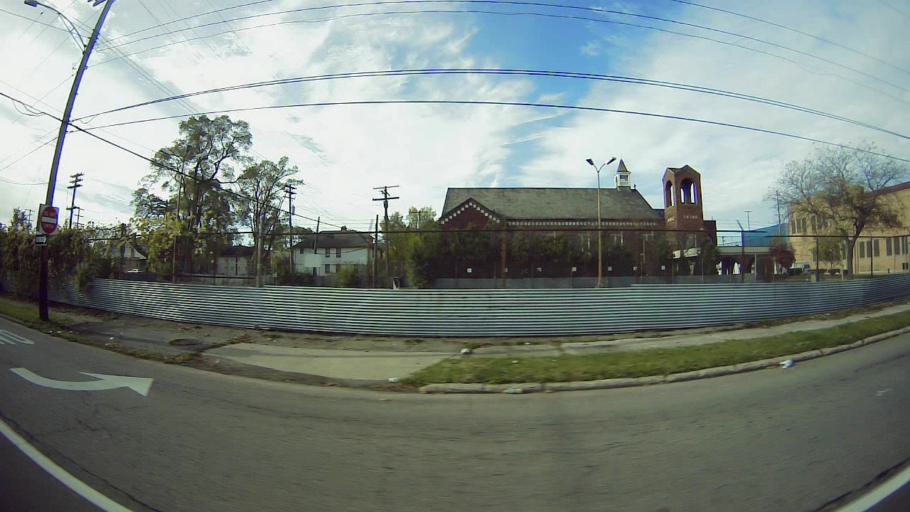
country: US
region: Michigan
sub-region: Wayne County
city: Highland Park
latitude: 42.4008
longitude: -83.1162
